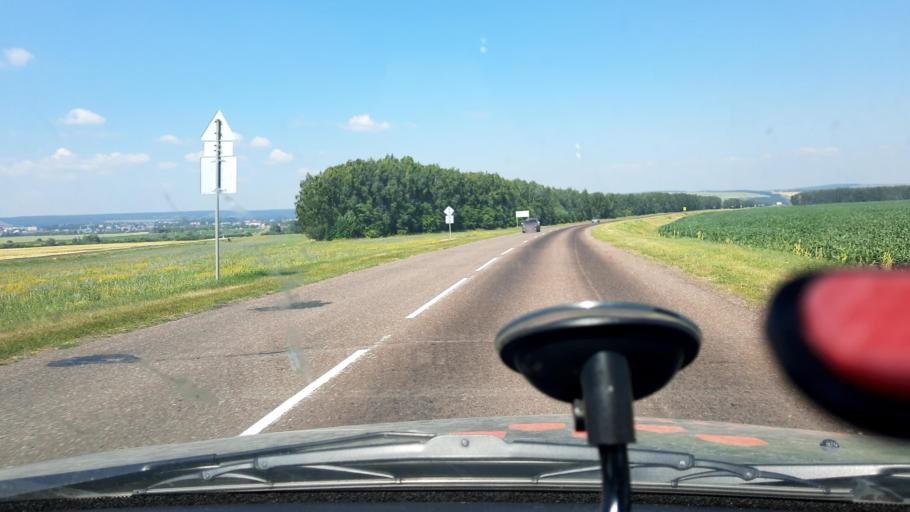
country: RU
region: Bashkortostan
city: Chekmagush
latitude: 55.1096
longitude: 54.6522
